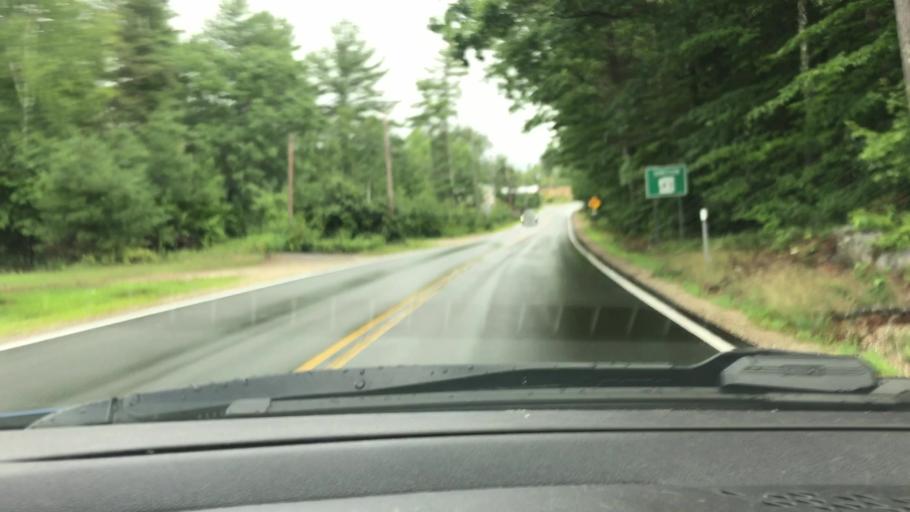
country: US
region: New Hampshire
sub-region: Rockingham County
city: Candia
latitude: 43.1551
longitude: -71.2347
